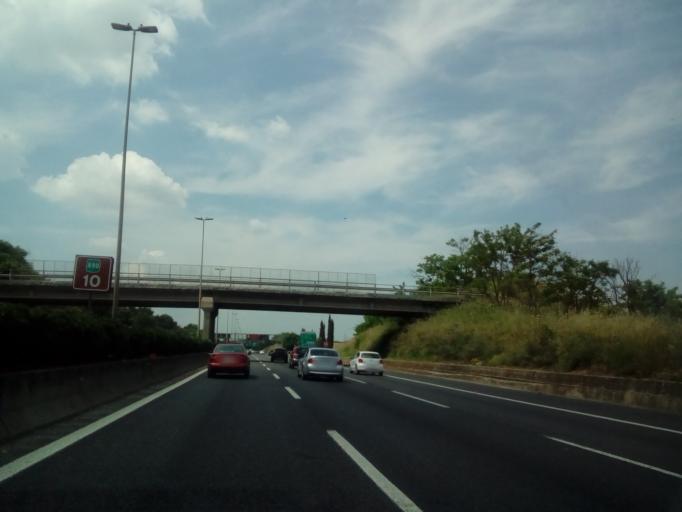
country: IT
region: Latium
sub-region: Citta metropolitana di Roma Capitale
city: Colle Verde
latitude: 41.9488
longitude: 12.5891
